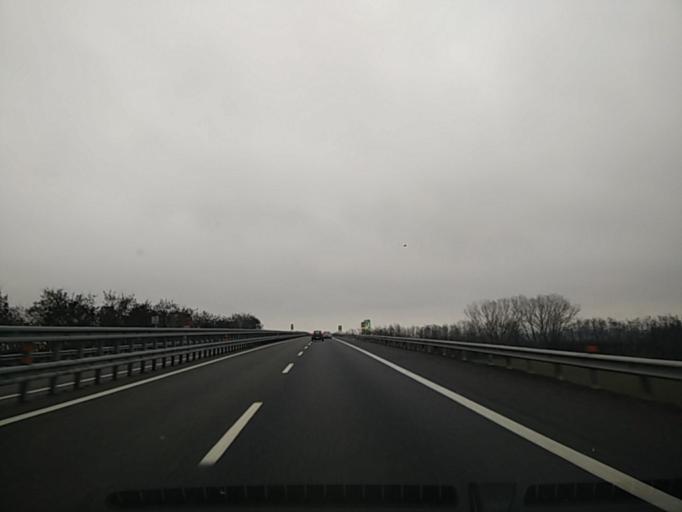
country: IT
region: Lombardy
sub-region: Provincia di Pavia
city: Pizzale
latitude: 45.0206
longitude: 9.0358
